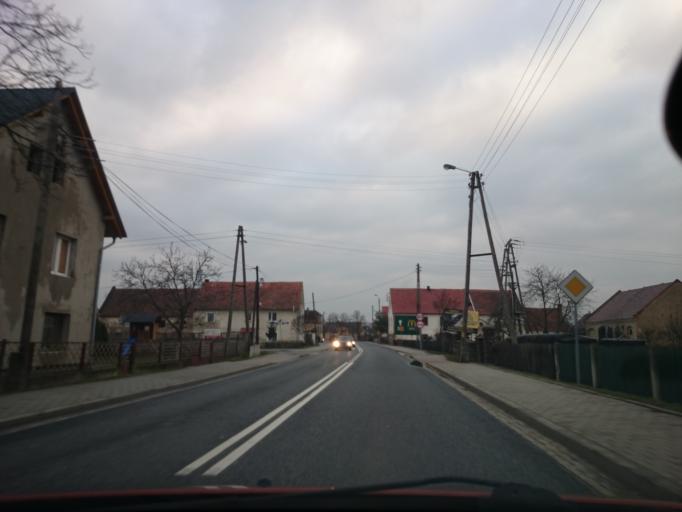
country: PL
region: Opole Voivodeship
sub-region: Powiat nyski
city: Sidzina
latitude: 50.5745
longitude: 17.4506
